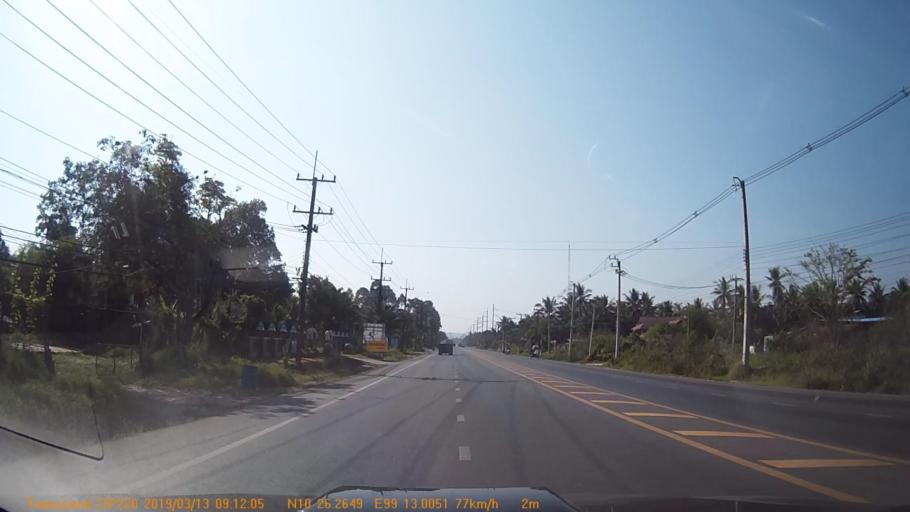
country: TH
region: Chumphon
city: Chumphon
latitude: 10.4374
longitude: 99.2169
